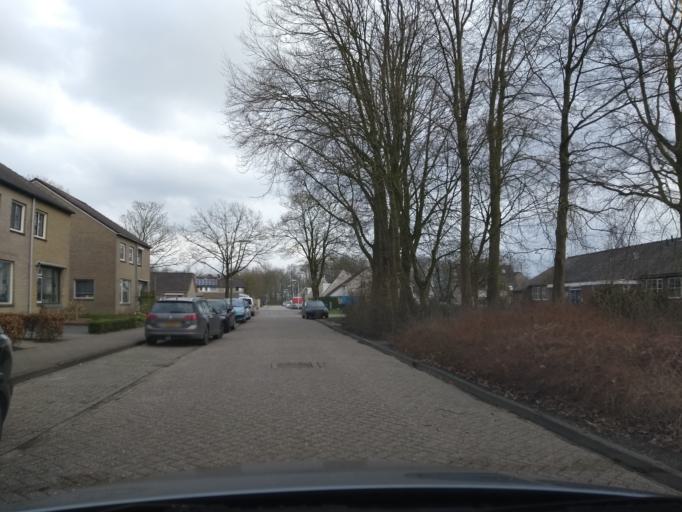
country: NL
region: Flevoland
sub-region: Gemeente Noordoostpolder
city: Ens
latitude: 52.7420
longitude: 5.8525
